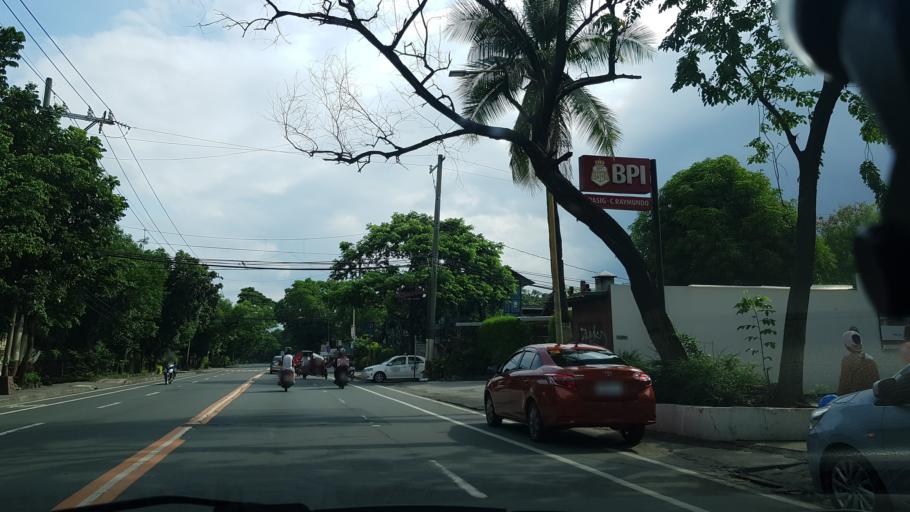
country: PH
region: Metro Manila
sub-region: Pasig
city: Pasig City
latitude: 14.5821
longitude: 121.0874
